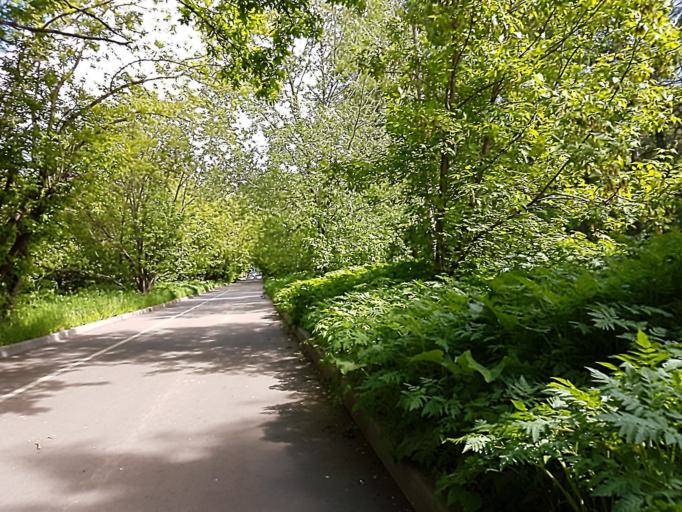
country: RU
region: Moscow
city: Perovo
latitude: 55.7401
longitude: 37.8062
